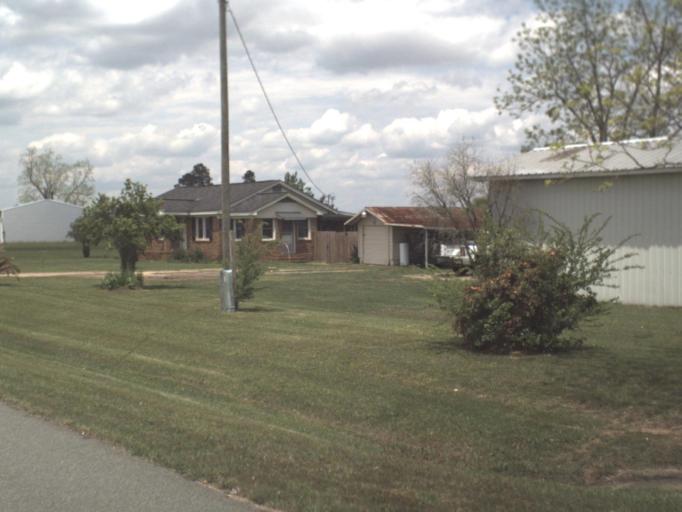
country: US
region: Alabama
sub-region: Escambia County
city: Atmore
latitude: 30.9720
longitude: -87.4879
